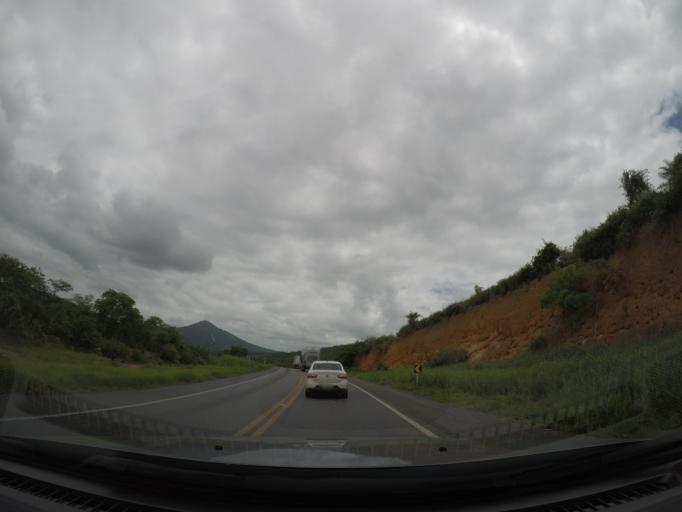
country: BR
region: Bahia
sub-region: Ruy Barbosa
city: Terra Nova
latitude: -12.4531
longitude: -40.5967
